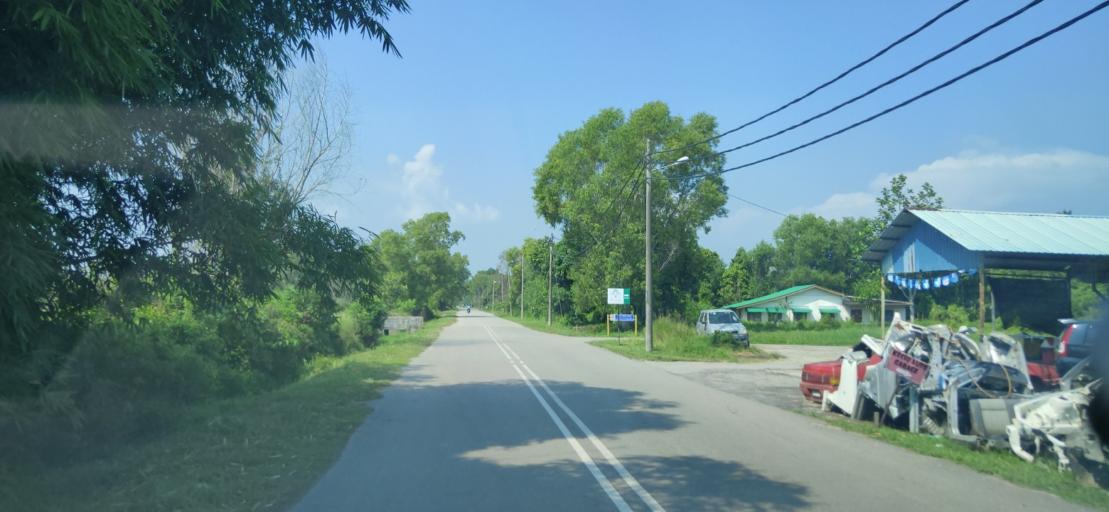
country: MY
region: Kedah
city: Sungai Petani
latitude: 5.6735
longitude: 100.4622
